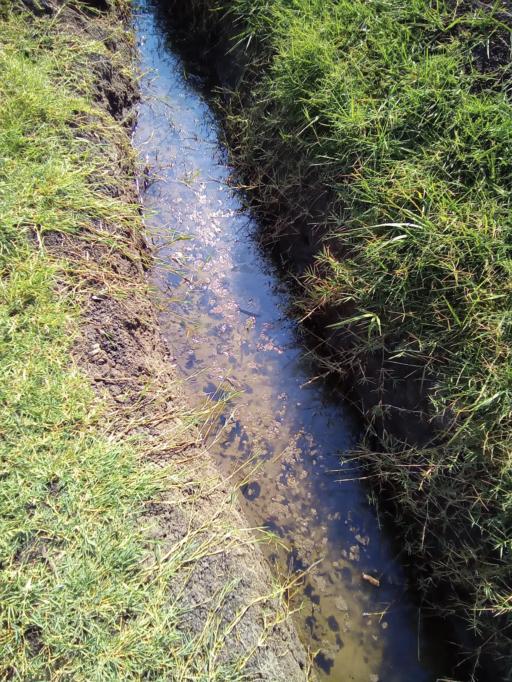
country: KE
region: Homa Bay
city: Homa Bay
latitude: -0.4642
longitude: 34.1830
